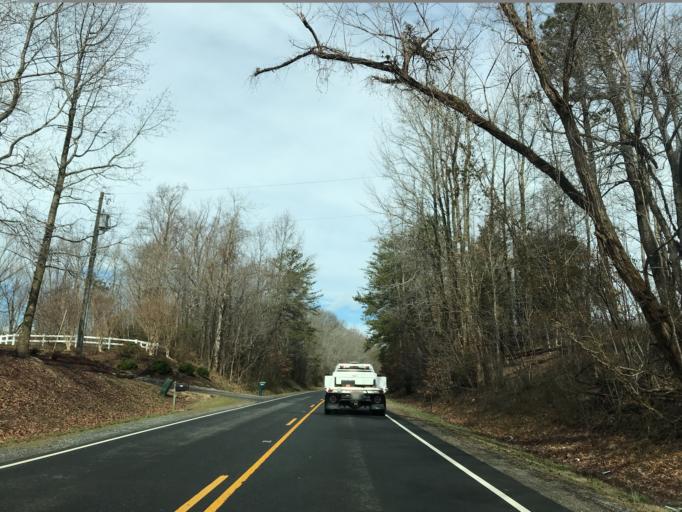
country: US
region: Virginia
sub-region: King George County
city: Dahlgren
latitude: 38.3133
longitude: -77.0786
